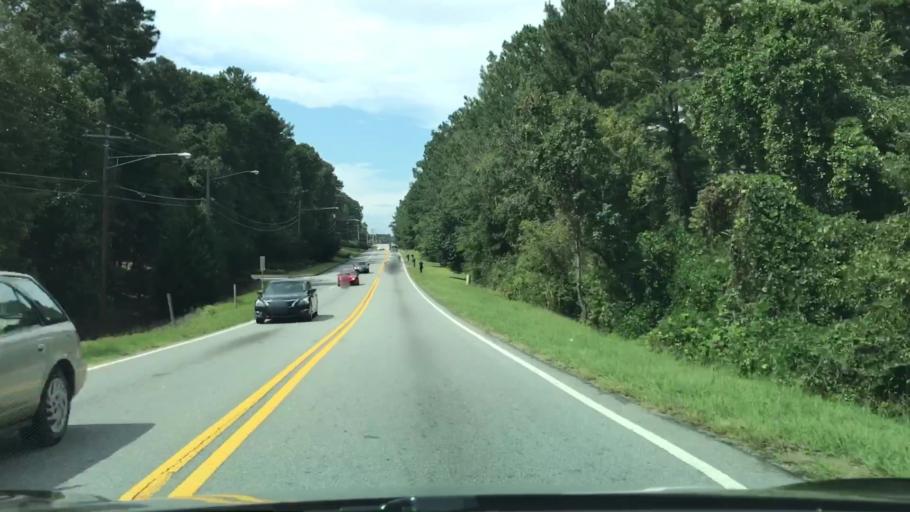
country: US
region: Georgia
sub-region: Gwinnett County
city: Snellville
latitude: 33.8804
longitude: -84.0558
